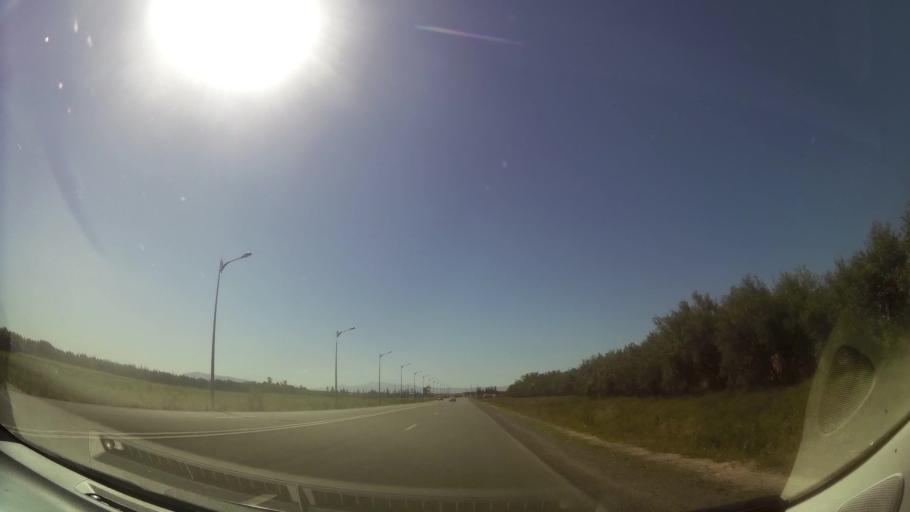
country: MA
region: Oriental
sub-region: Oujda-Angad
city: Oujda
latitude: 34.7366
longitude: -1.8807
